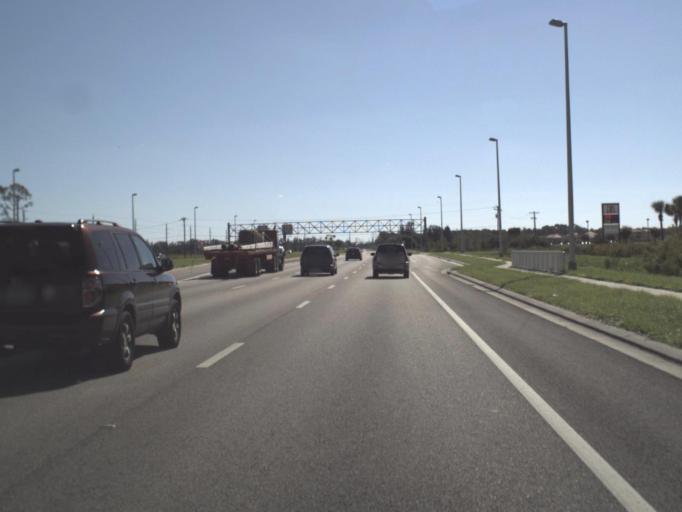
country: US
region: Florida
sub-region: Lee County
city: Fort Myers
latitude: 26.6340
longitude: -81.8002
